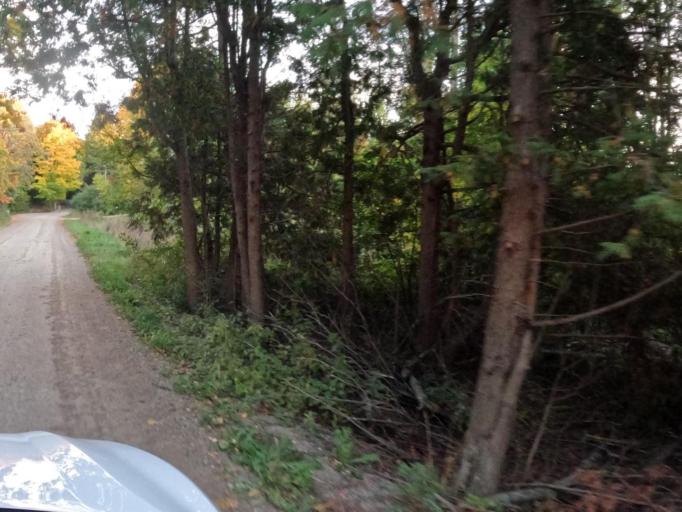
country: CA
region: Ontario
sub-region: Wellington County
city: Guelph
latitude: 43.5656
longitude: -80.1667
